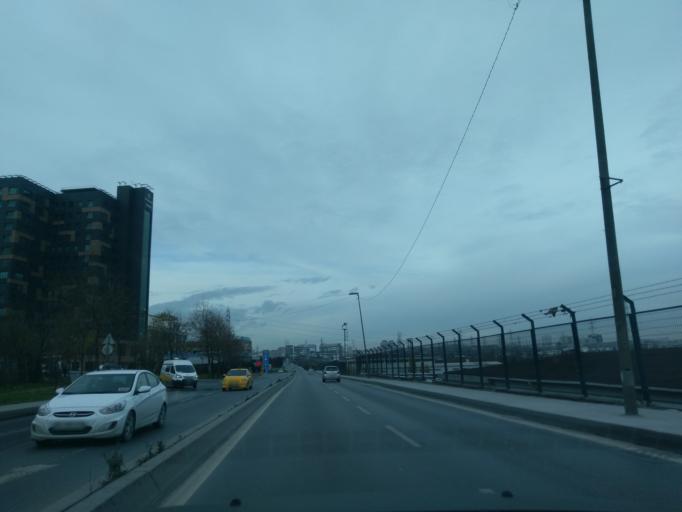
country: TR
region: Istanbul
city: Mahmutbey
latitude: 41.0592
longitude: 28.7904
